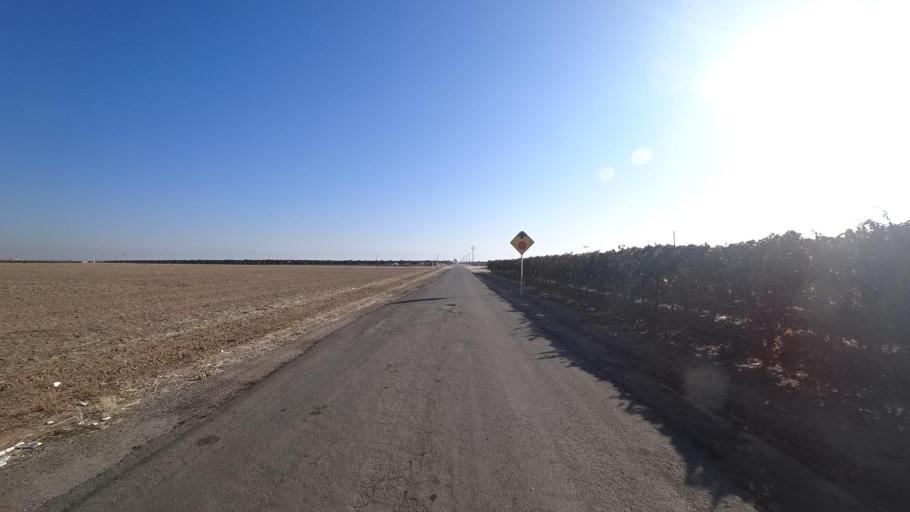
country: US
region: California
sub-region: Kern County
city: McFarland
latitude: 35.7252
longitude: -119.1572
